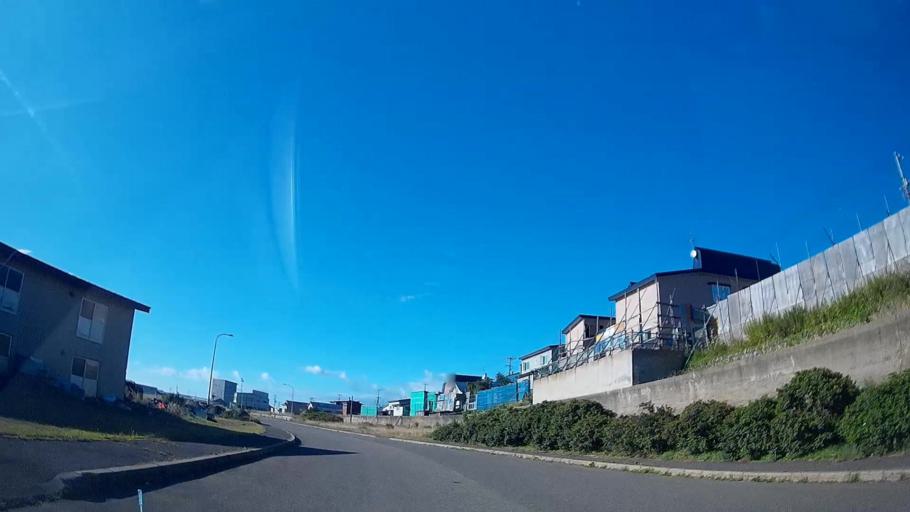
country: JP
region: Hokkaido
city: Iwanai
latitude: 42.4536
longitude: 139.8487
